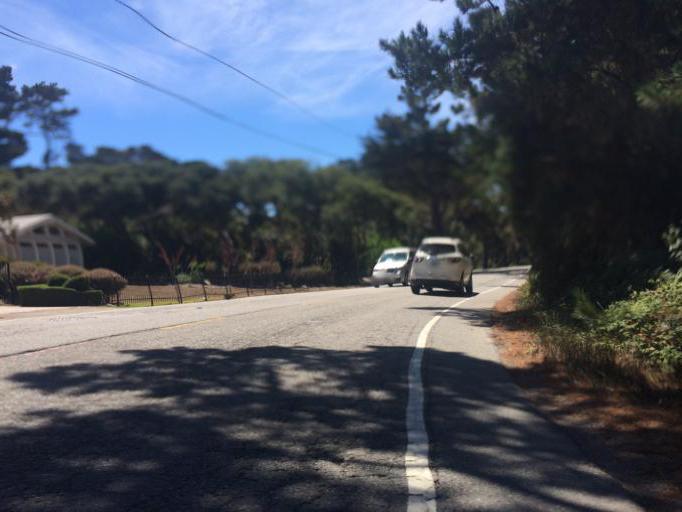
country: US
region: California
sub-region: Monterey County
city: Del Monte Forest
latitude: 36.6084
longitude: -121.9422
